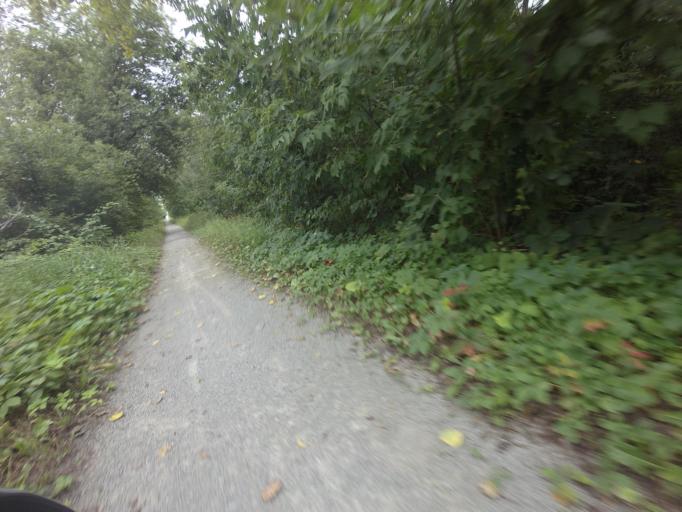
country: CA
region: Ontario
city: Uxbridge
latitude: 44.3079
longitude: -78.8921
